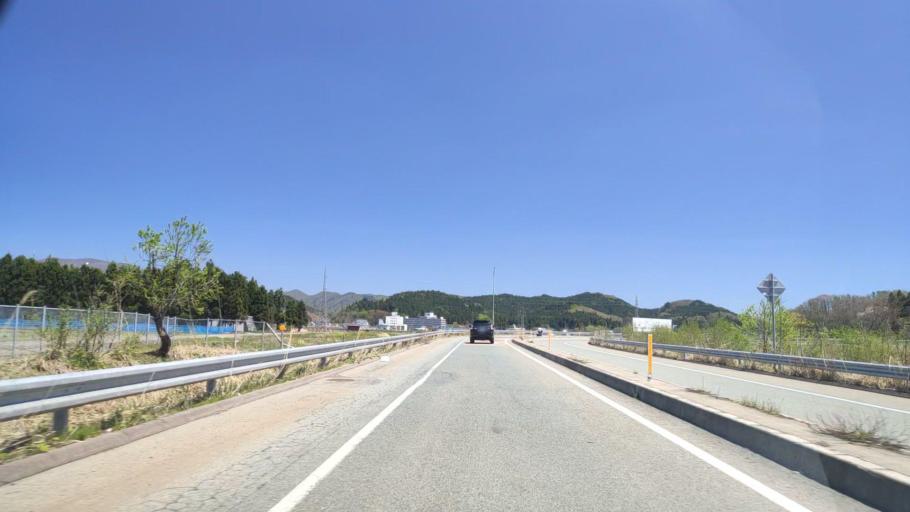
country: JP
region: Yamagata
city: Shinjo
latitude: 38.7394
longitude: 140.2986
